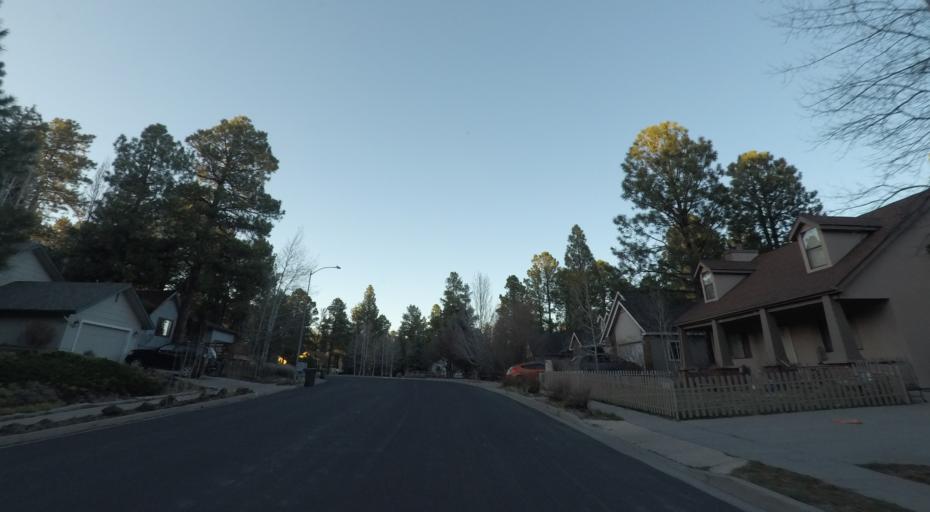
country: US
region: Arizona
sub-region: Coconino County
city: Flagstaff
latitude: 35.1755
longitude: -111.6791
